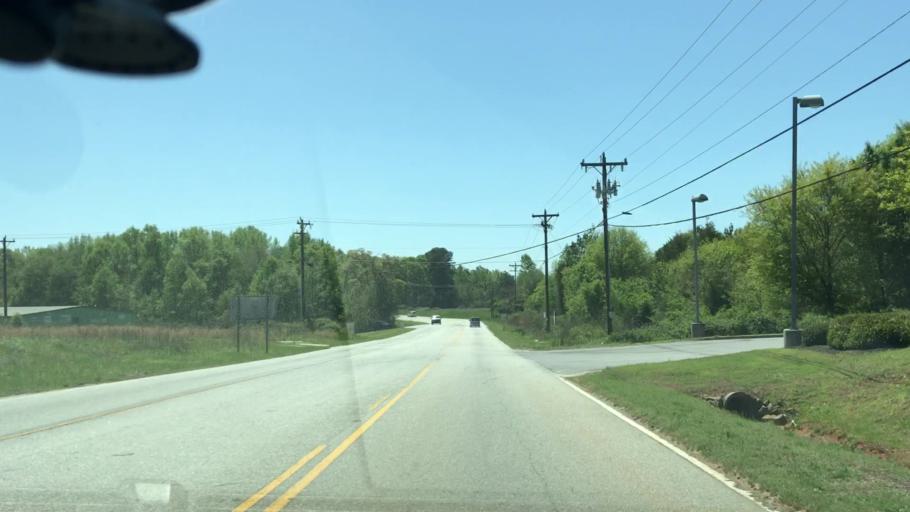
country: US
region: South Carolina
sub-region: Greenville County
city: Mauldin
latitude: 34.7505
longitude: -82.2898
